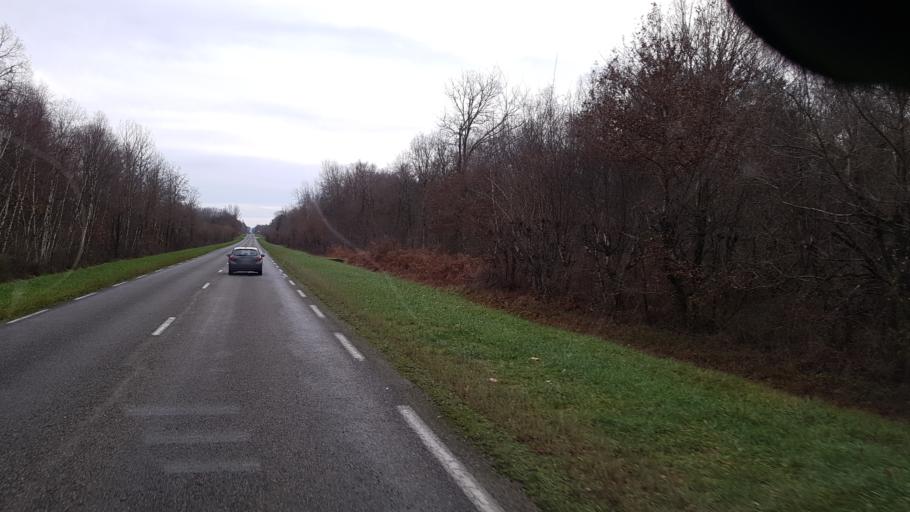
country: FR
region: Centre
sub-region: Departement du Loiret
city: La Ferte-Saint-Aubin
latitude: 47.6974
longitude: 1.9513
